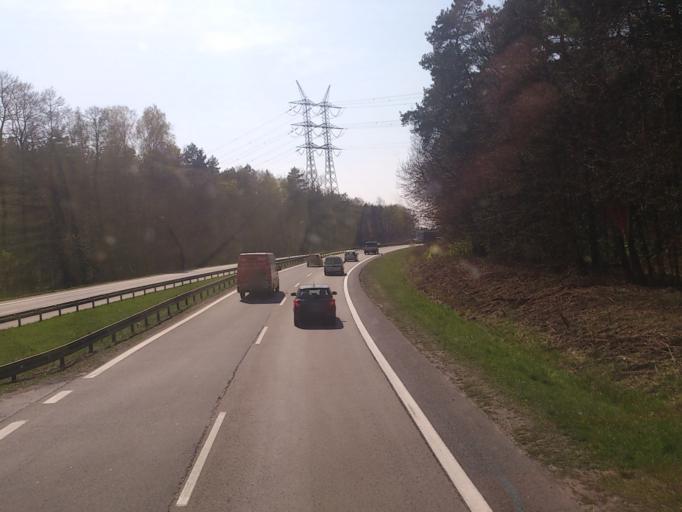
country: PL
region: Silesian Voivodeship
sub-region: Powiat bedzinski
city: Sarnow
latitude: 50.3856
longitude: 19.1806
